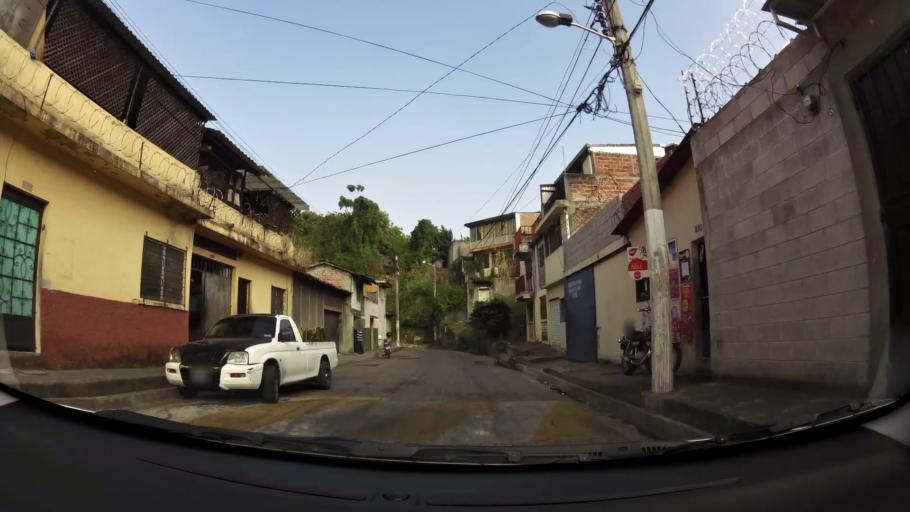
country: SV
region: San Salvador
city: San Salvador
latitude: 13.6975
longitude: -89.1827
